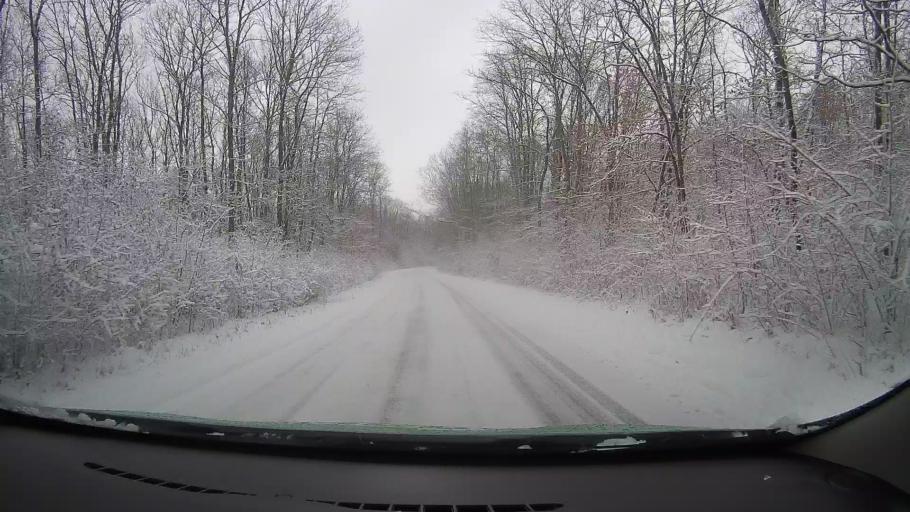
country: RO
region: Hunedoara
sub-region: Comuna Pestisu Mic
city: Pestisu Mic
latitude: 45.8124
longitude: 22.9013
